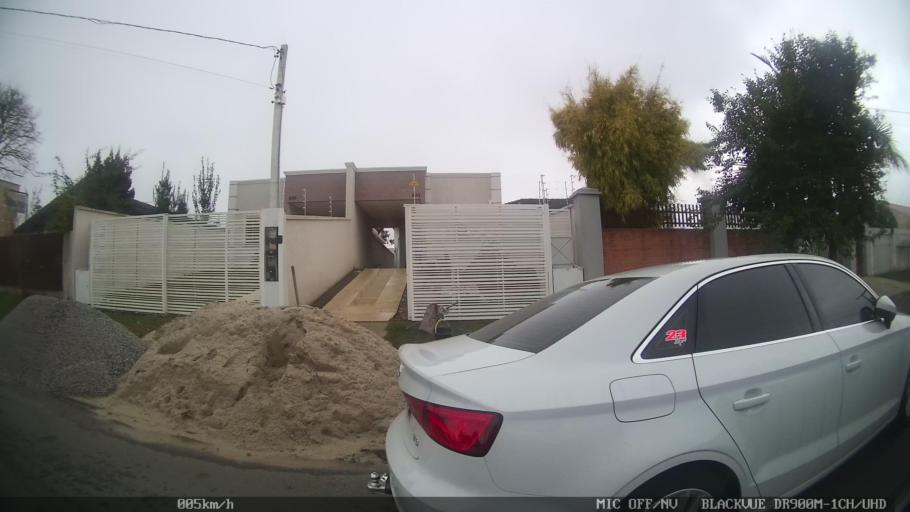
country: BR
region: Parana
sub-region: Sao Jose Dos Pinhais
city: Sao Jose dos Pinhais
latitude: -25.6068
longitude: -49.1668
